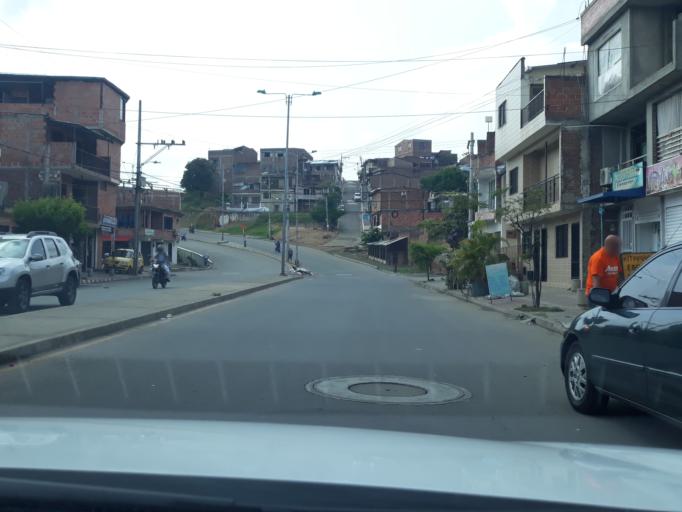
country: CO
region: Valle del Cauca
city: Cali
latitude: 3.3898
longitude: -76.5566
